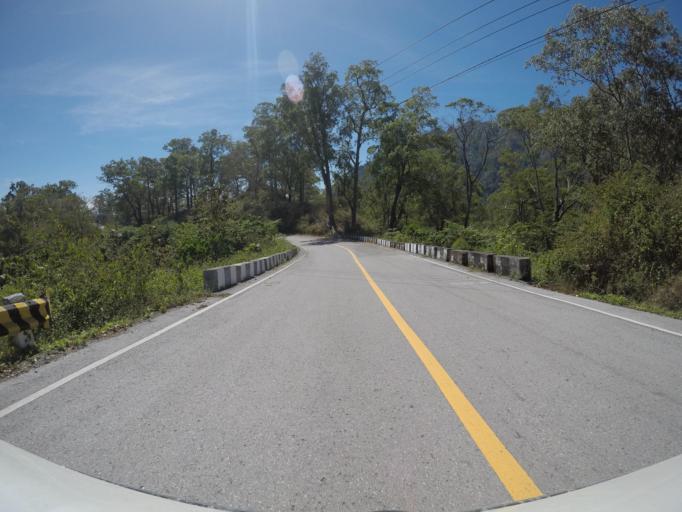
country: TL
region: Manufahi
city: Same
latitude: -8.8905
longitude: 125.9835
